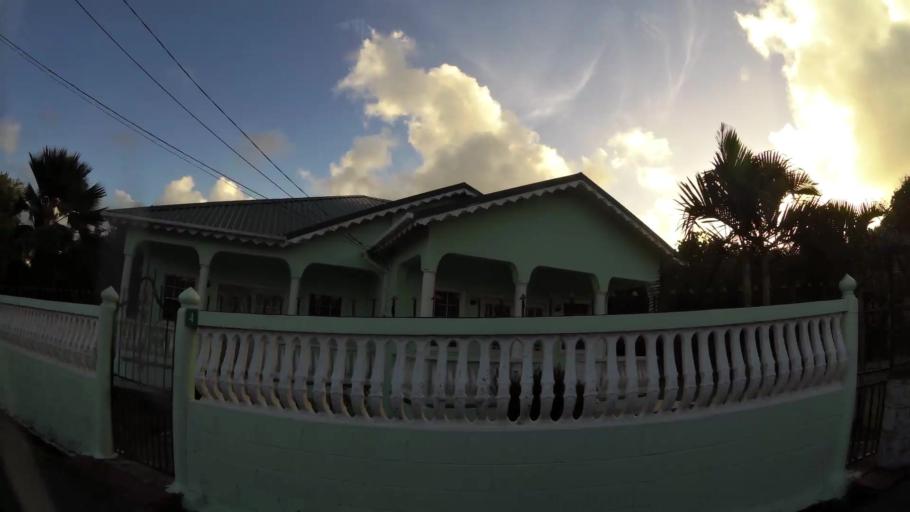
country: LC
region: Gros-Islet
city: Gros Islet
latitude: 14.0706
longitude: -60.9364
